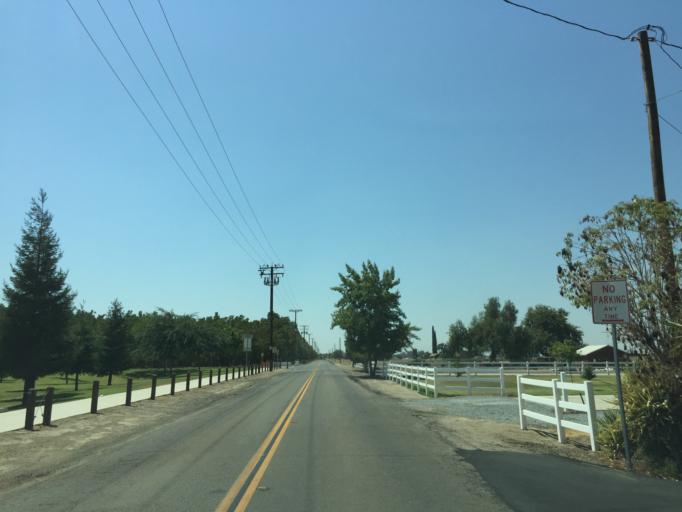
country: US
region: California
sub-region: Tulare County
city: Visalia
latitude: 36.3637
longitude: -119.3044
